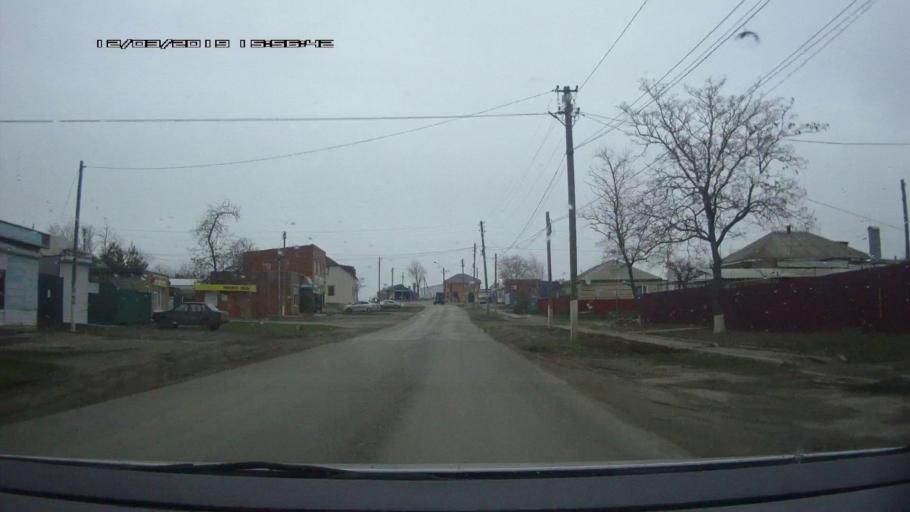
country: RU
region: Rostov
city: Novobataysk
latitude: 46.9018
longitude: 39.7817
